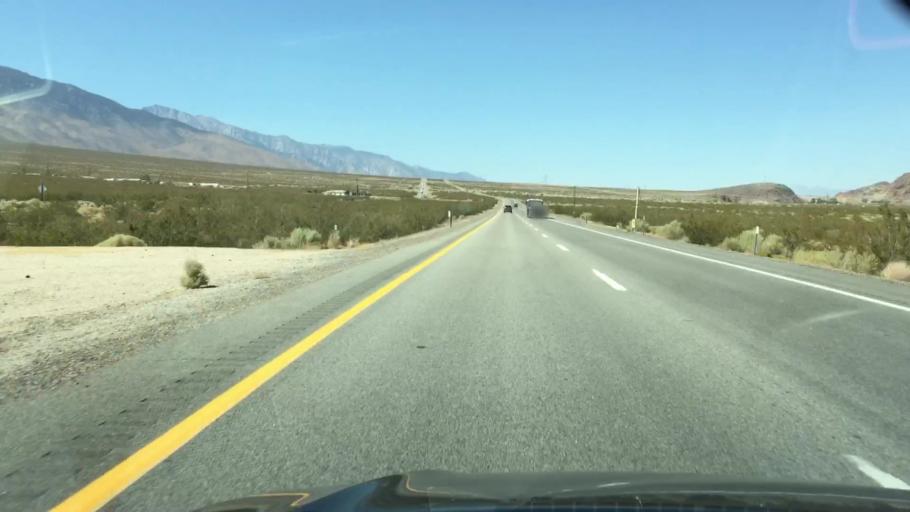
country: US
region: California
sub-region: Kern County
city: Inyokern
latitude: 36.0821
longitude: -117.9587
